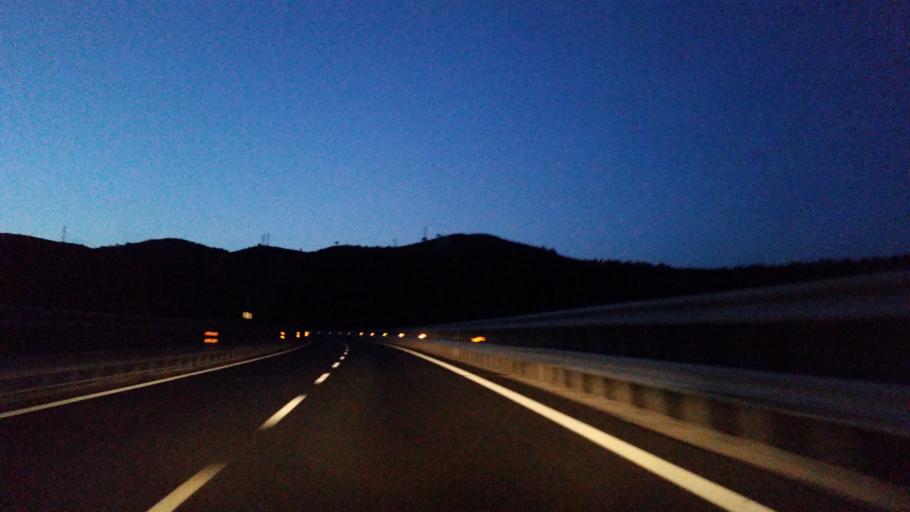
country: IT
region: Liguria
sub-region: Provincia di Savona
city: Laigueglia
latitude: 43.9916
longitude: 8.1371
